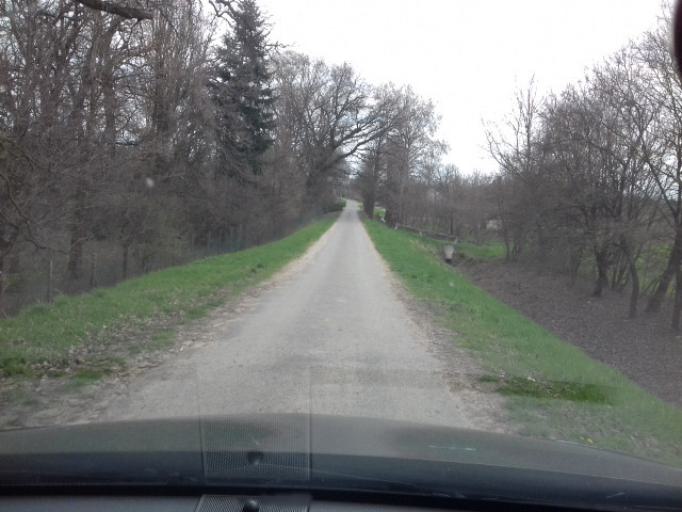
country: HU
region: Bacs-Kiskun
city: Tiszakecske
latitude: 46.8888
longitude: 20.1166
